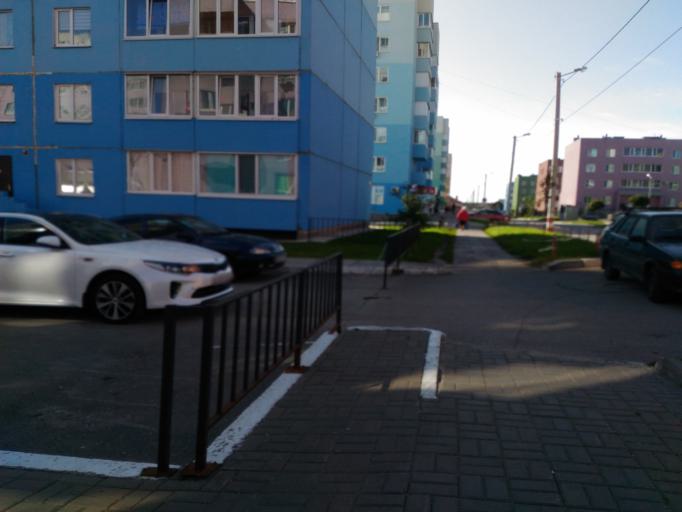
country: RU
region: Ulyanovsk
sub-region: Ulyanovskiy Rayon
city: Ulyanovsk
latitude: 54.3482
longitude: 48.3406
